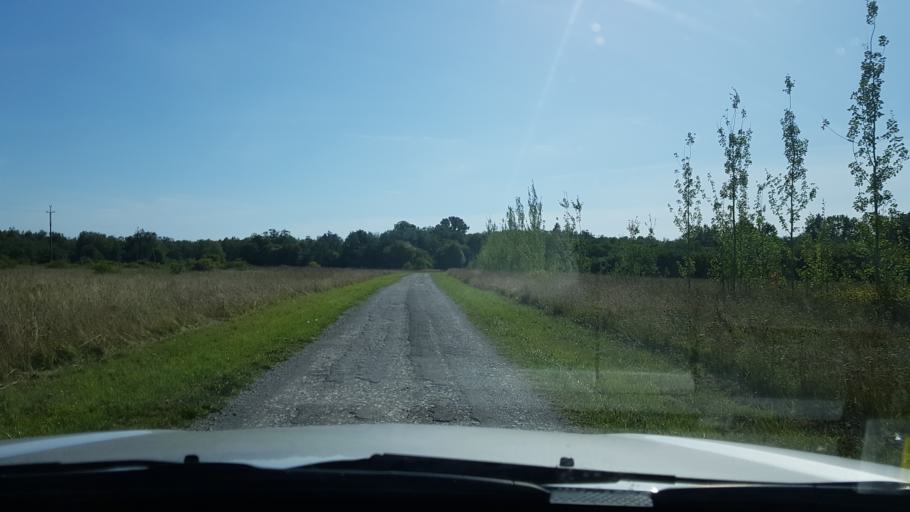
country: EE
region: Ida-Virumaa
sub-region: Sillamaee linn
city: Sillamae
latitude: 59.3919
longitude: 27.8774
